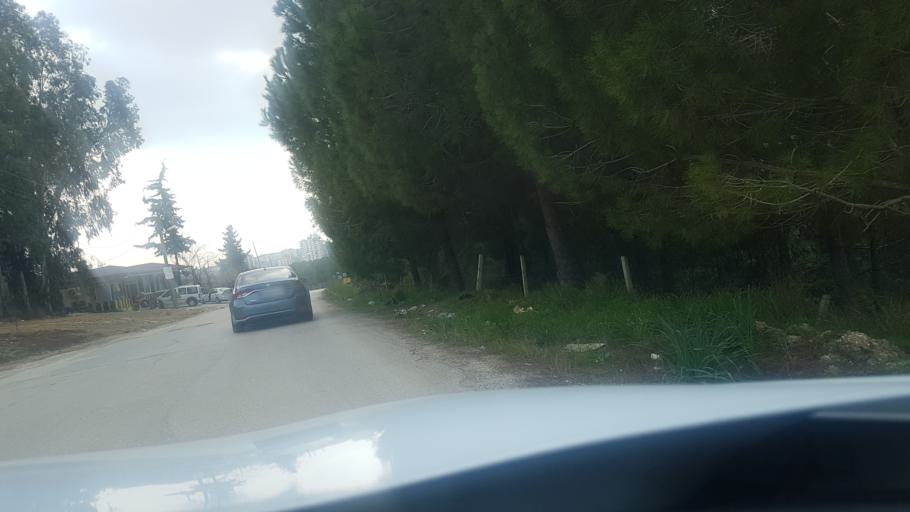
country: TR
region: Adana
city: Seyhan
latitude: 37.0593
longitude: 35.2565
